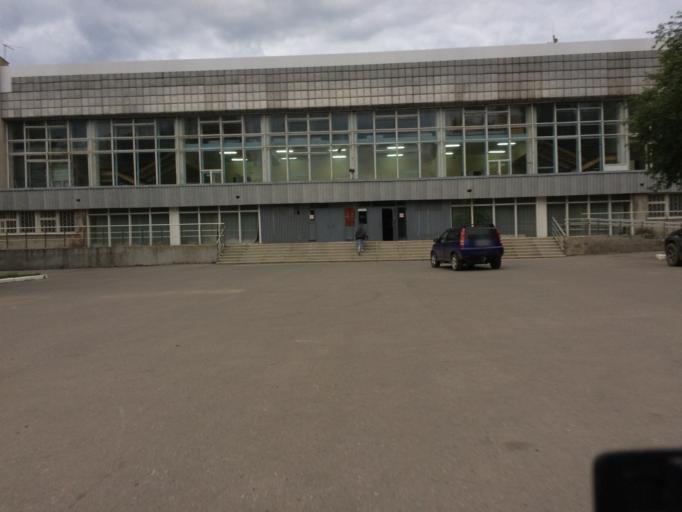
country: RU
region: Mariy-El
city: Yoshkar-Ola
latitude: 56.6235
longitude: 47.8863
